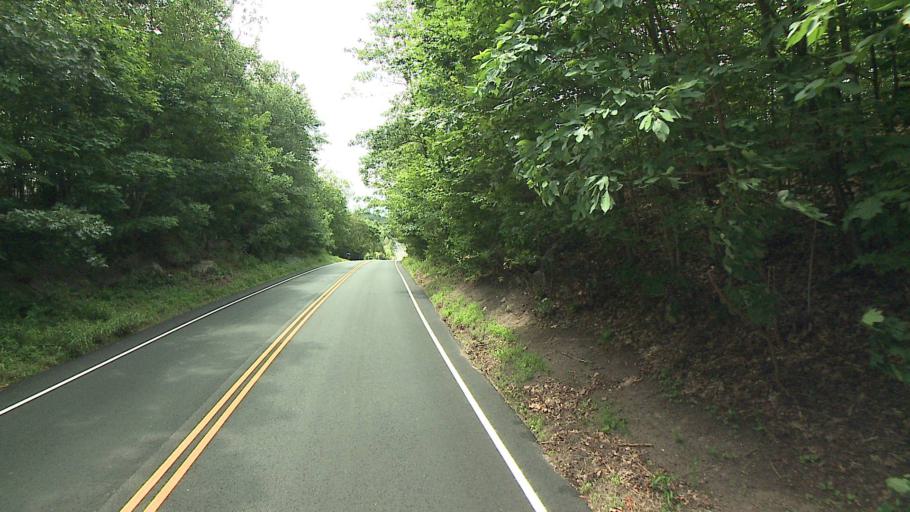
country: US
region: Massachusetts
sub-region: Hampden County
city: Granville
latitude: 42.0304
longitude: -72.8856
